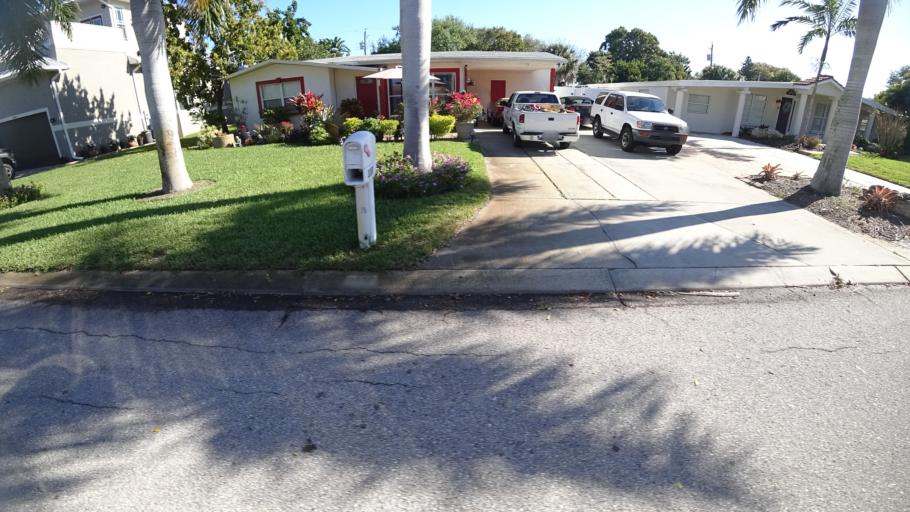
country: US
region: Florida
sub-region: Manatee County
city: Bayshore Gardens
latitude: 27.4223
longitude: -82.5938
